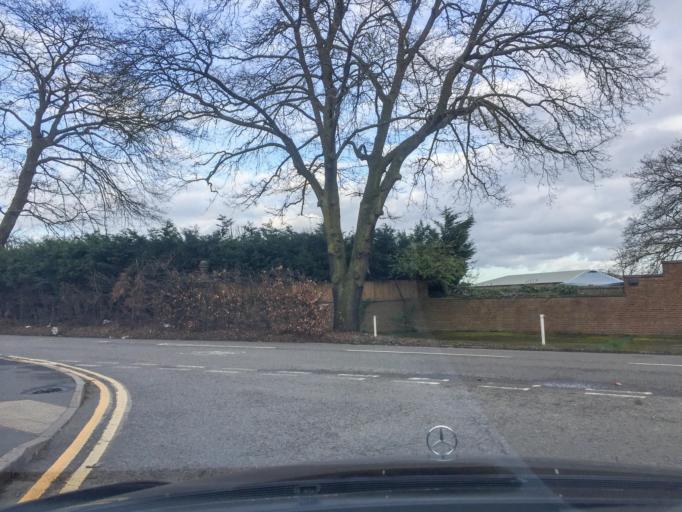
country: GB
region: England
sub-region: City and Borough of Birmingham
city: Birmingham
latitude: 52.4521
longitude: -1.9262
